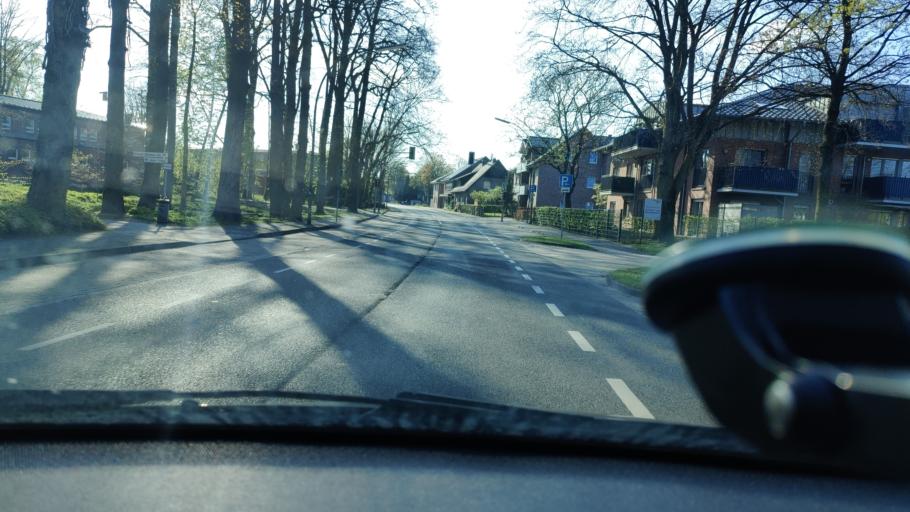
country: DE
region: North Rhine-Westphalia
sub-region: Regierungsbezirk Munster
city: Gescher
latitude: 51.9574
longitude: 7.0039
